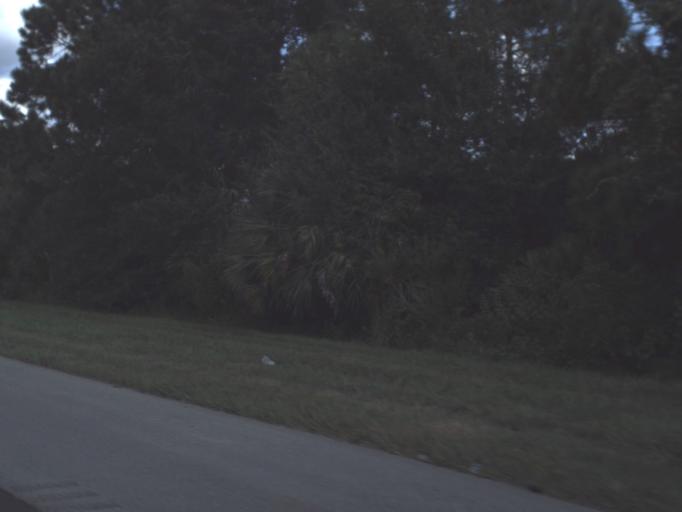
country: US
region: Florida
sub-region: Sarasota County
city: Nokomis
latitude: 27.1252
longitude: -82.3975
